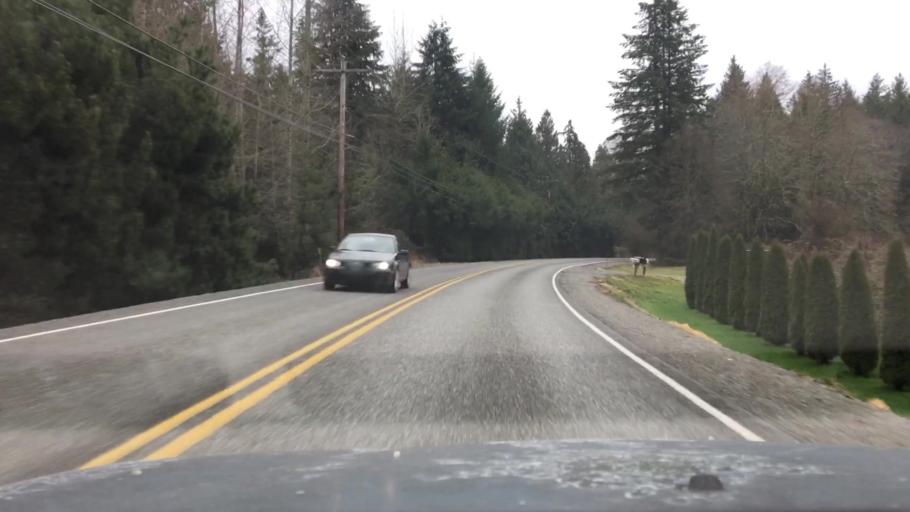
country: US
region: Washington
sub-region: Whatcom County
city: Sudden Valley
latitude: 48.6371
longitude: -122.3113
